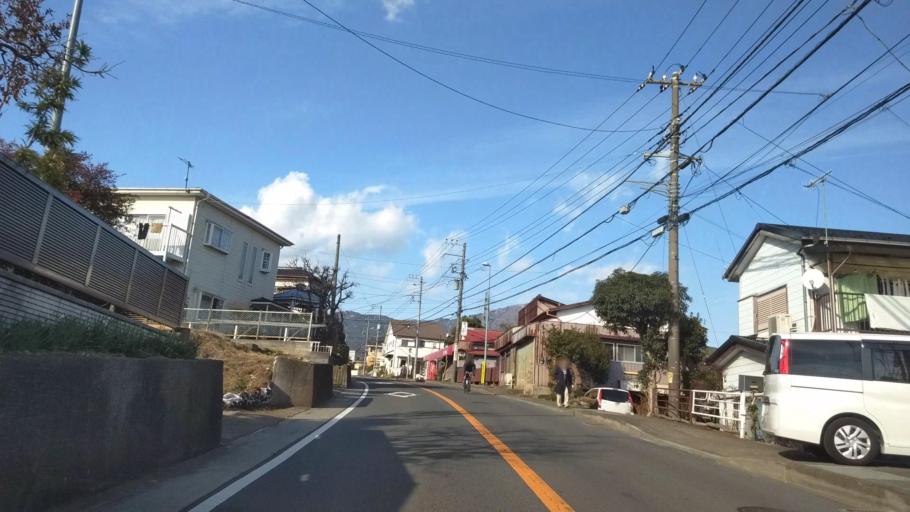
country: JP
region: Kanagawa
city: Hadano
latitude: 35.3847
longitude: 139.2376
